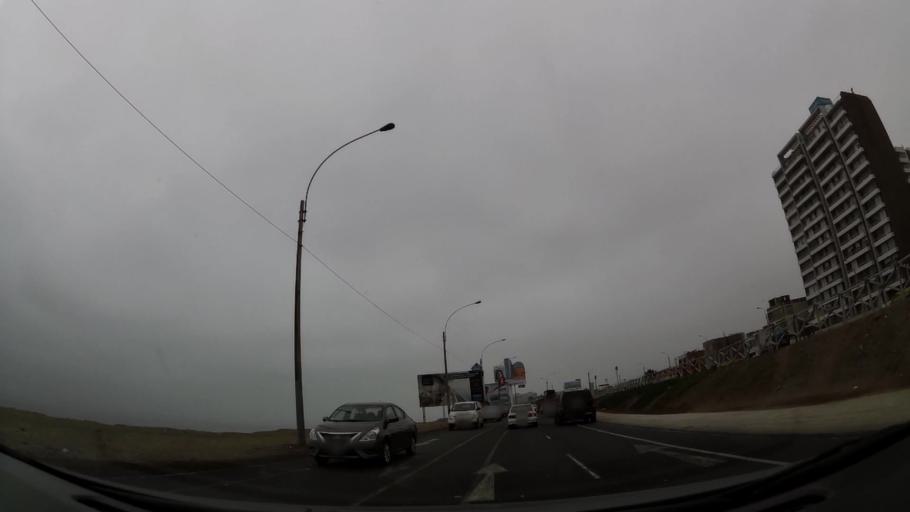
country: PE
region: Callao
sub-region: Callao
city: Callao
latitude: -12.0871
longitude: -77.0943
